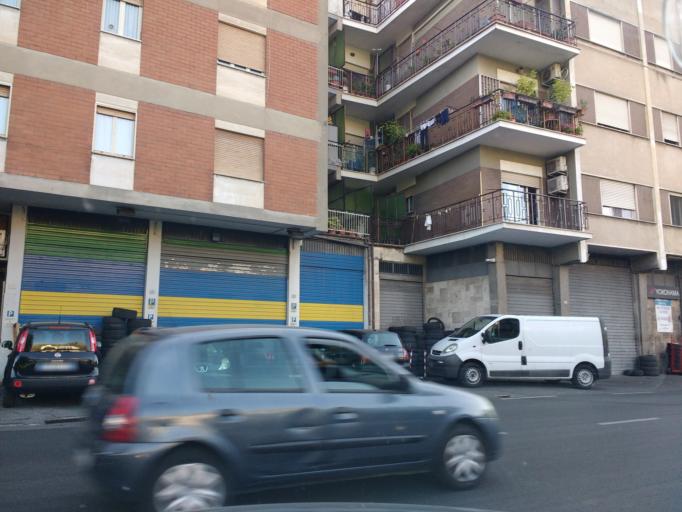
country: IT
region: Latium
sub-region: Citta metropolitana di Roma Capitale
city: Tivoli
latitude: 41.9627
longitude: 12.8022
